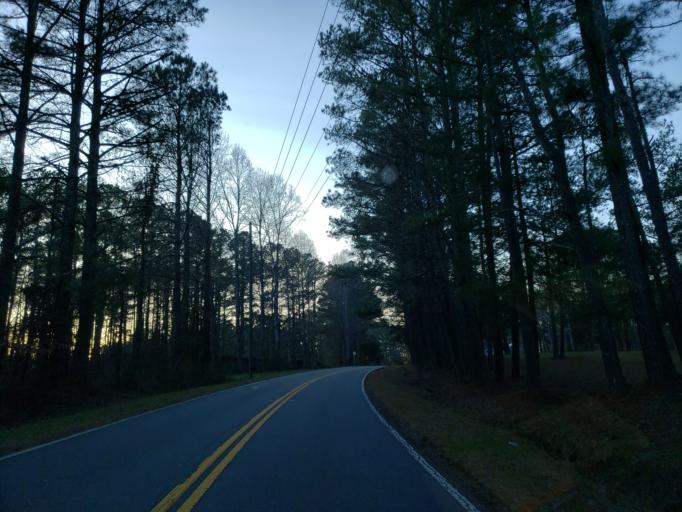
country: US
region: Georgia
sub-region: Cobb County
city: Acworth
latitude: 34.0167
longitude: -84.7351
